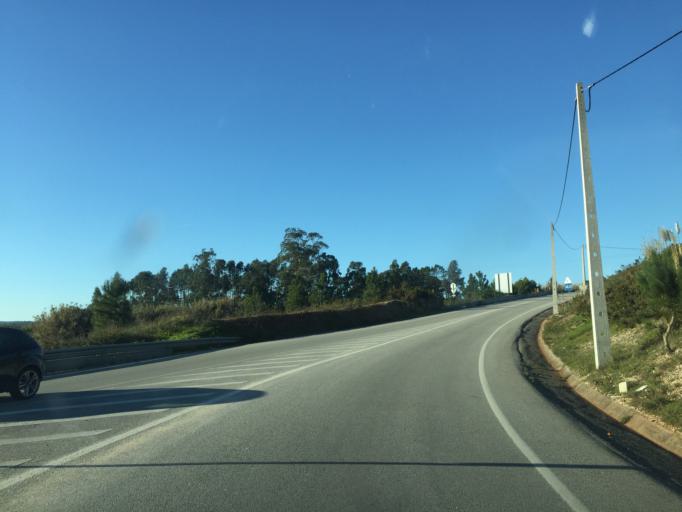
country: PT
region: Coimbra
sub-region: Figueira da Foz
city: Alhadas
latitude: 40.1769
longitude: -8.7985
